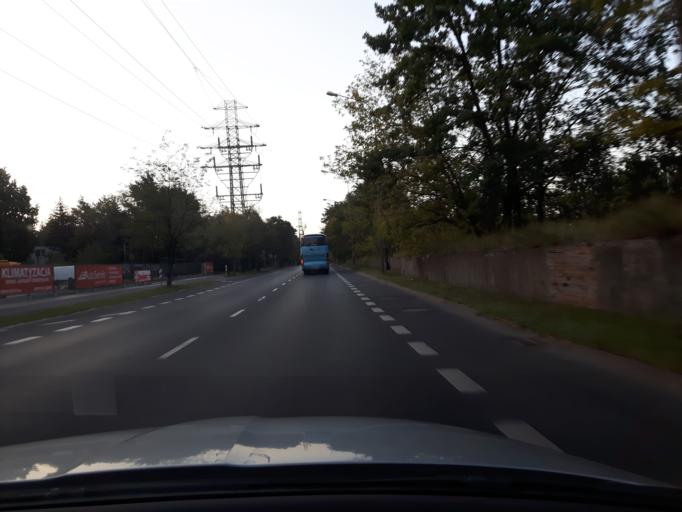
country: PL
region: Masovian Voivodeship
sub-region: Warszawa
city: Wawer
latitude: 52.2117
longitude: 21.1618
